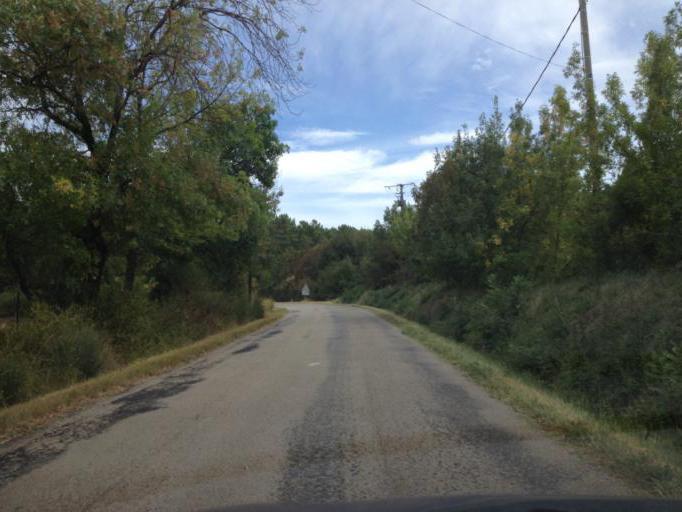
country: FR
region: Rhone-Alpes
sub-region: Departement de la Drome
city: Allan
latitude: 44.4819
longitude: 4.7993
